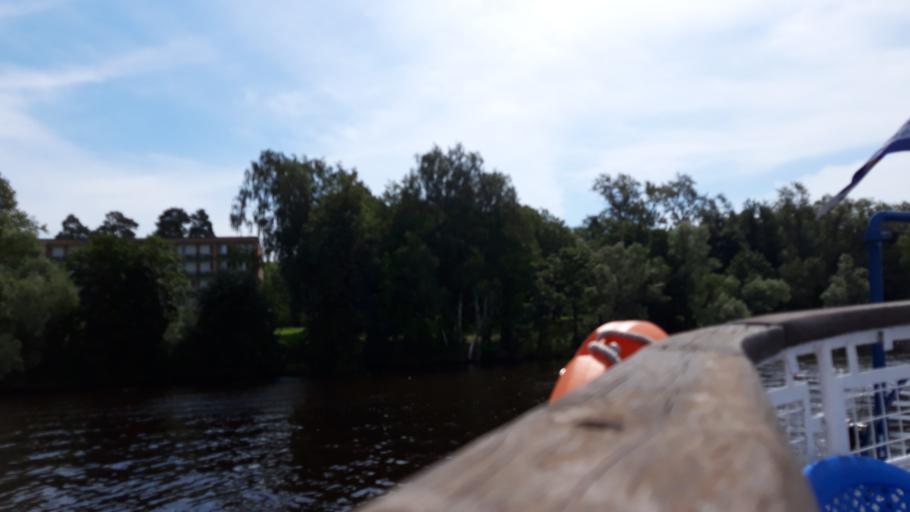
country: RU
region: Tverskaya
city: Konakovo
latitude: 56.6904
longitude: 36.6977
